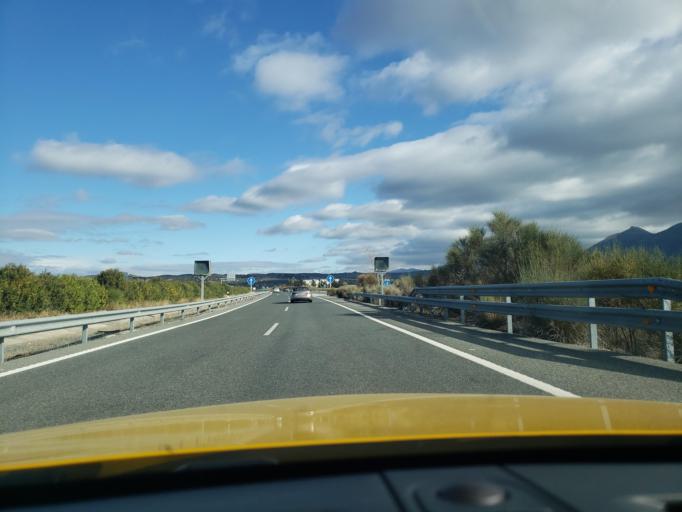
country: ES
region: Andalusia
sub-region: Provincia de Malaga
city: Villanueva del Trabuco
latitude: 37.0682
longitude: -4.3276
